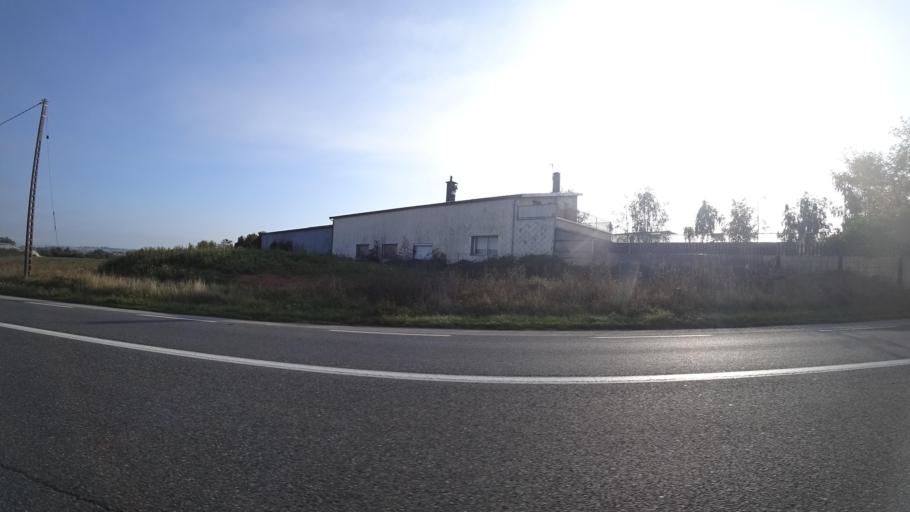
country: FR
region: Midi-Pyrenees
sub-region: Departement de l'Aveyron
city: Luc-la-Primaube
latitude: 44.3191
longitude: 2.5582
